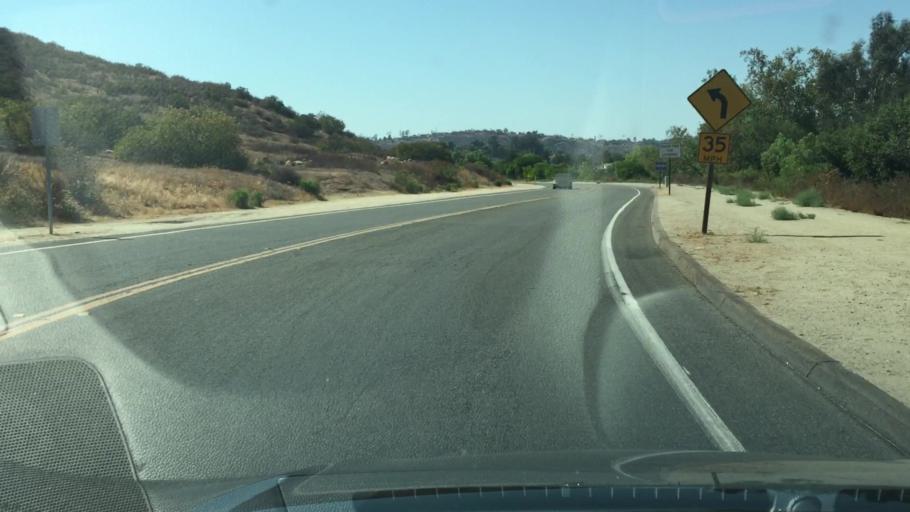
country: US
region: California
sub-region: San Diego County
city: Jamul
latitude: 32.7372
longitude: -116.8934
